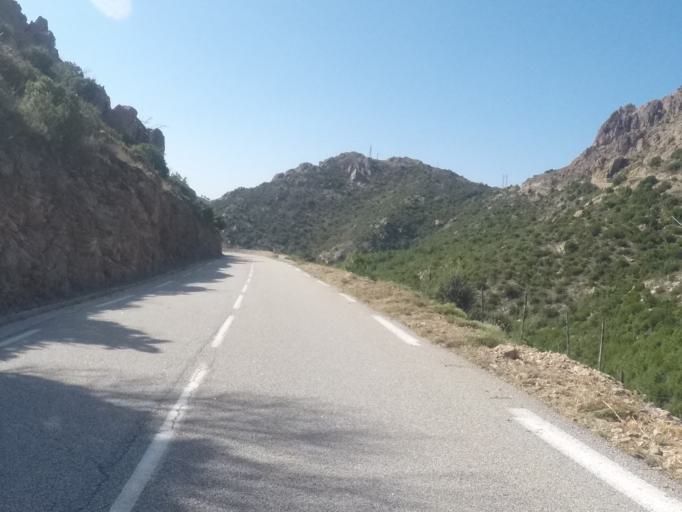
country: FR
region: Corsica
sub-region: Departement de la Corse-du-Sud
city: Zonza
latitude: 41.7703
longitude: 9.0457
